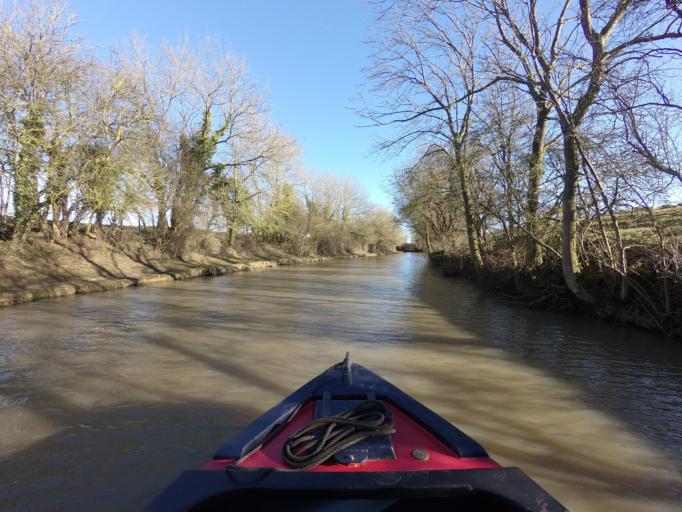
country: GB
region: England
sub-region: Northamptonshire
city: Bugbrooke
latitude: 52.2018
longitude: -1.0014
